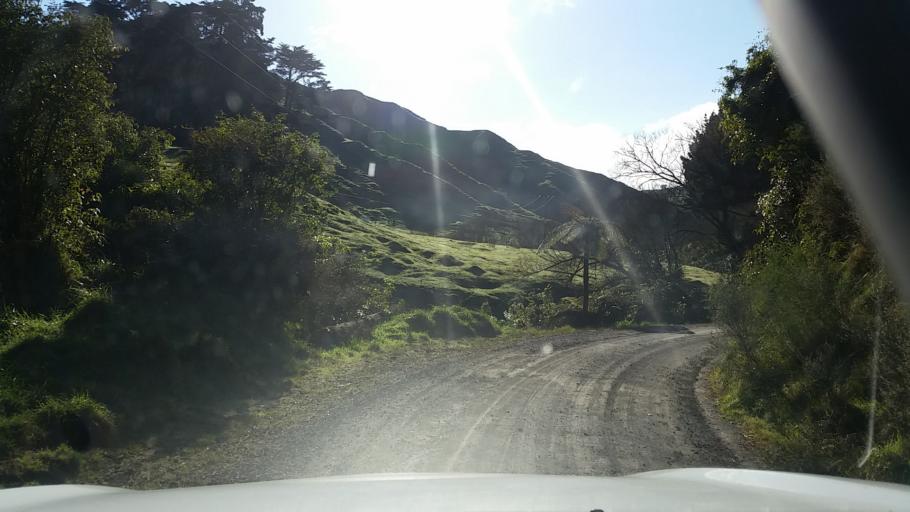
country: NZ
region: Taranaki
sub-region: South Taranaki District
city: Eltham
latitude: -39.5062
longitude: 174.3985
